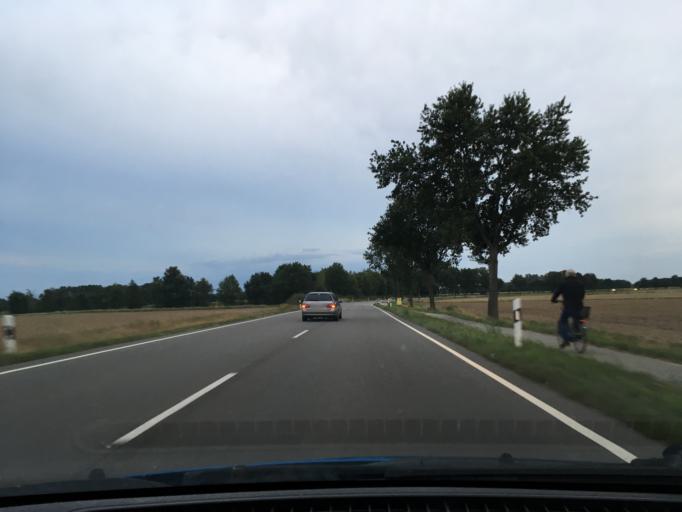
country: DE
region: Lower Saxony
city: Artlenburg
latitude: 53.3583
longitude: 10.4709
